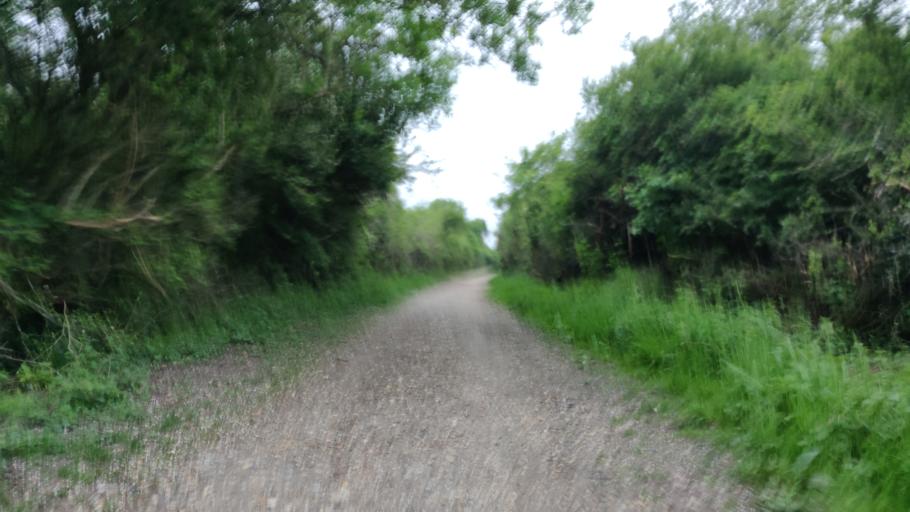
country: GB
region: England
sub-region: West Sussex
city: Partridge Green
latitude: 50.9960
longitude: -0.3166
